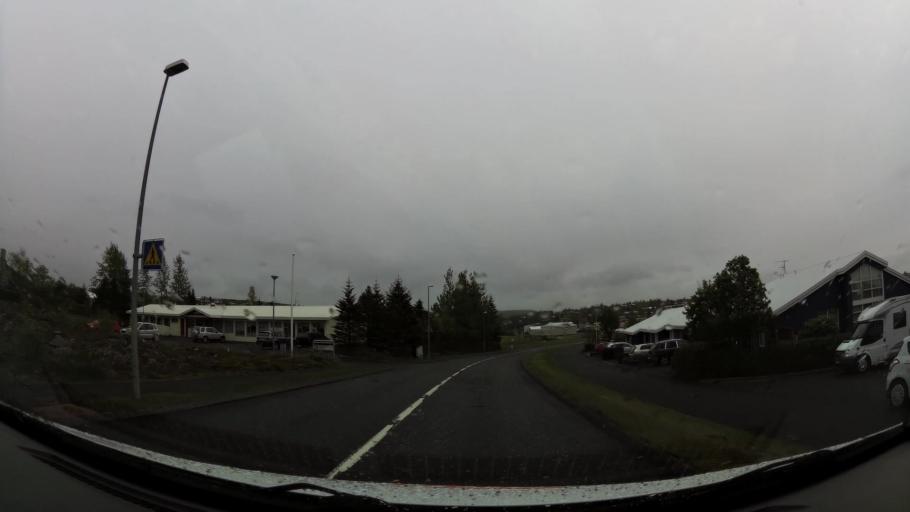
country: IS
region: Capital Region
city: Kopavogur
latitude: 64.0956
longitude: -21.8998
